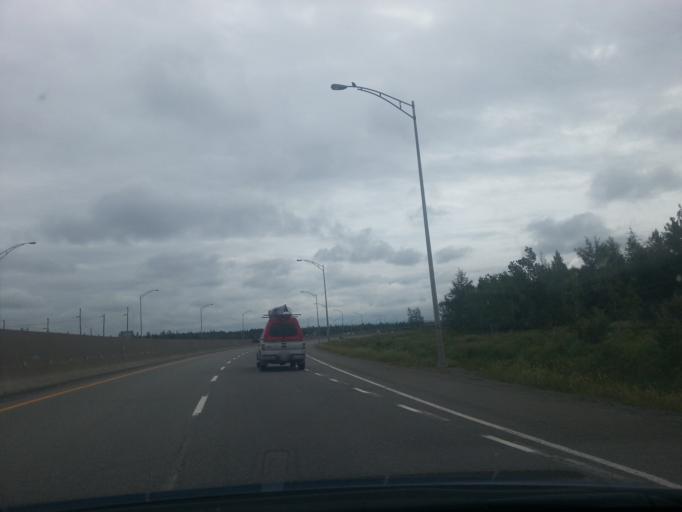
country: CA
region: Quebec
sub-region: Bas-Saint-Laurent
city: Riviere-du-Loup
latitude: 47.8129
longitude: -69.5228
